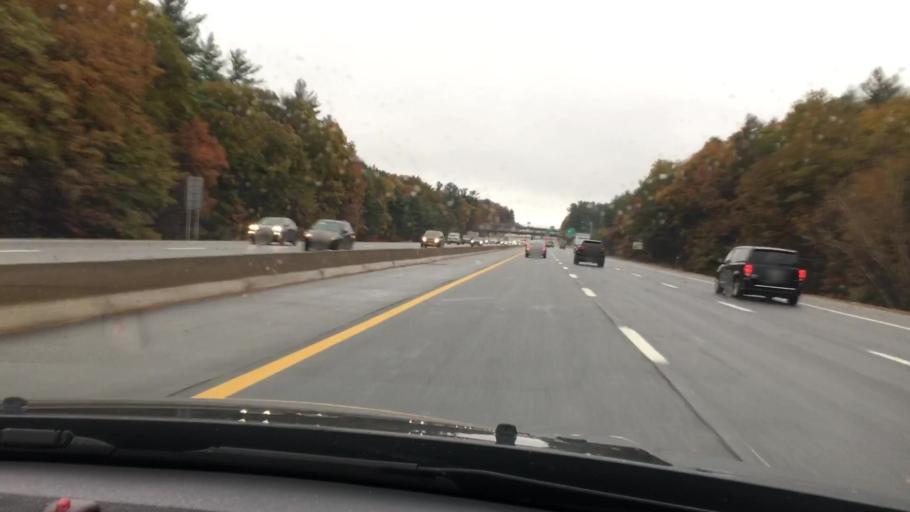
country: US
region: New Hampshire
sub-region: Hillsborough County
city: Nashua
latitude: 42.7960
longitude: -71.4972
